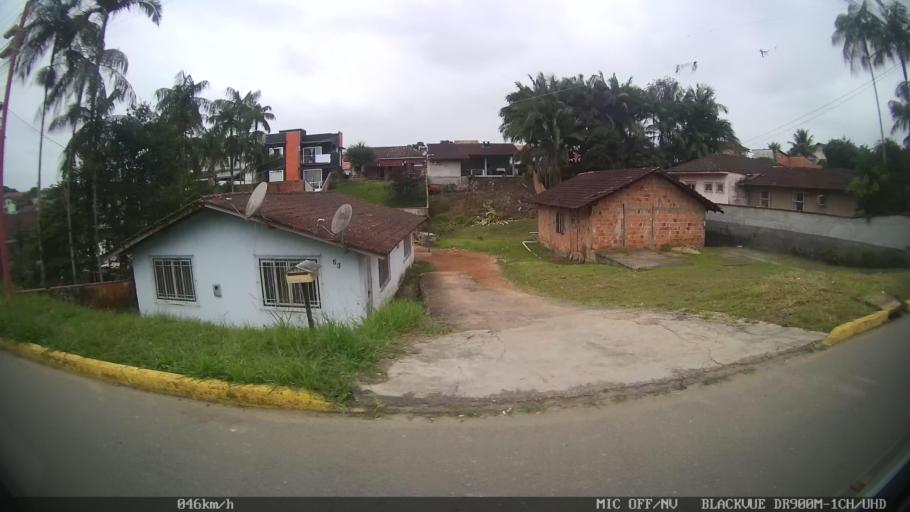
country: BR
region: Santa Catarina
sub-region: Joinville
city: Joinville
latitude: -26.3556
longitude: -48.8388
